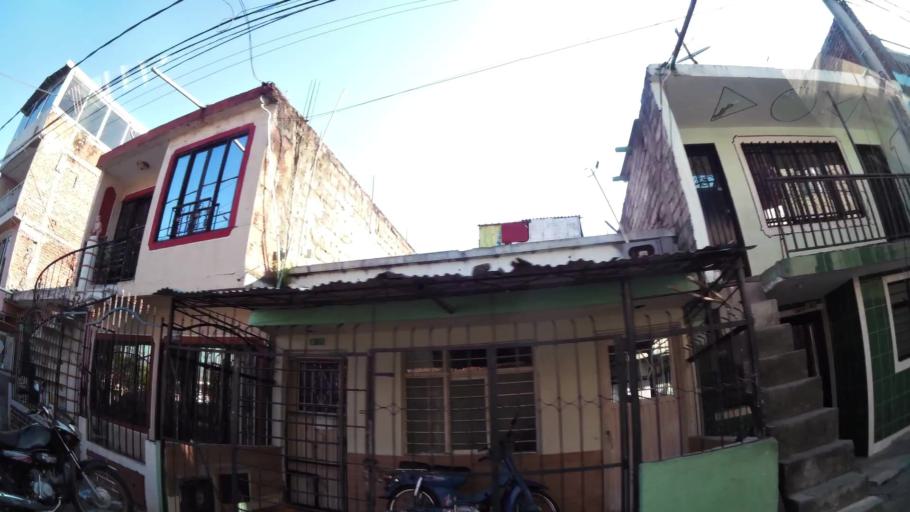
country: CO
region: Valle del Cauca
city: Cali
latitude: 3.4283
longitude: -76.5085
